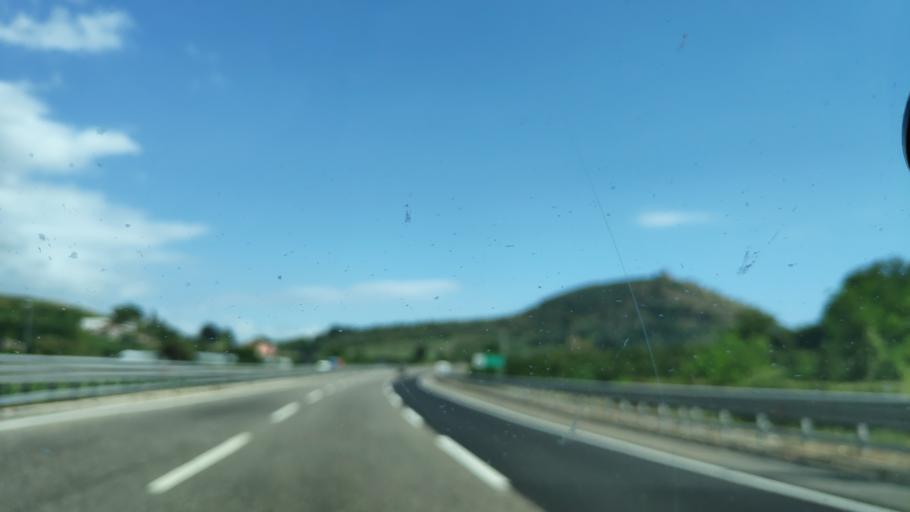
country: IT
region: Campania
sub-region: Provincia di Salerno
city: Pezzano-Filetta
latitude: 40.6847
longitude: 14.8534
